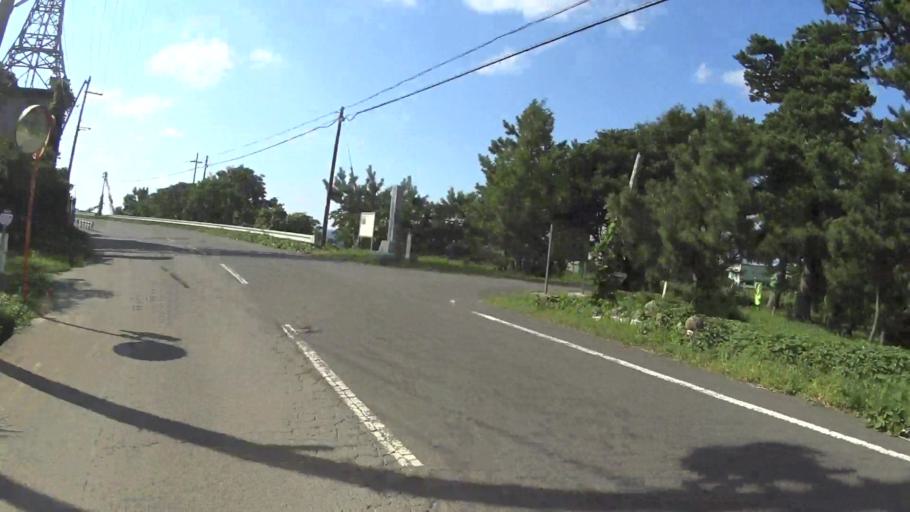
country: JP
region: Kyoto
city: Miyazu
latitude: 35.7645
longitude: 135.1948
